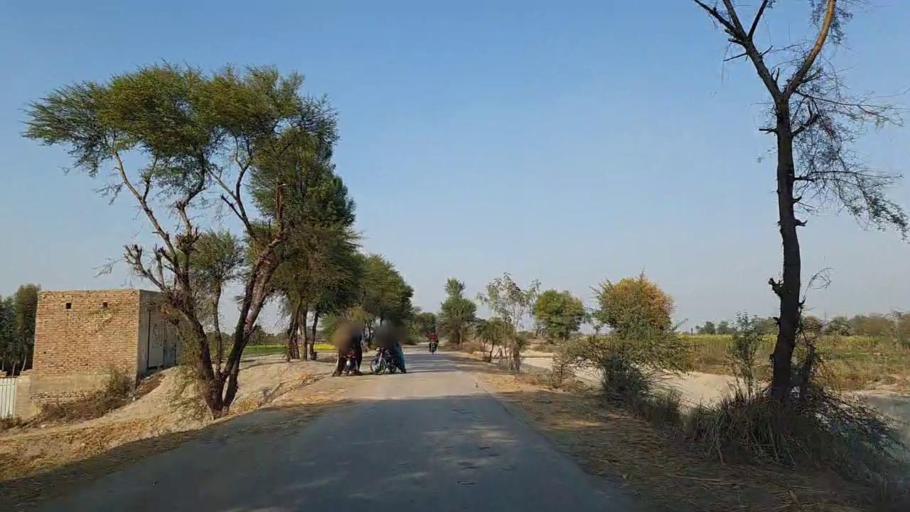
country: PK
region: Sindh
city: Daur
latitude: 26.4151
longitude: 68.2593
